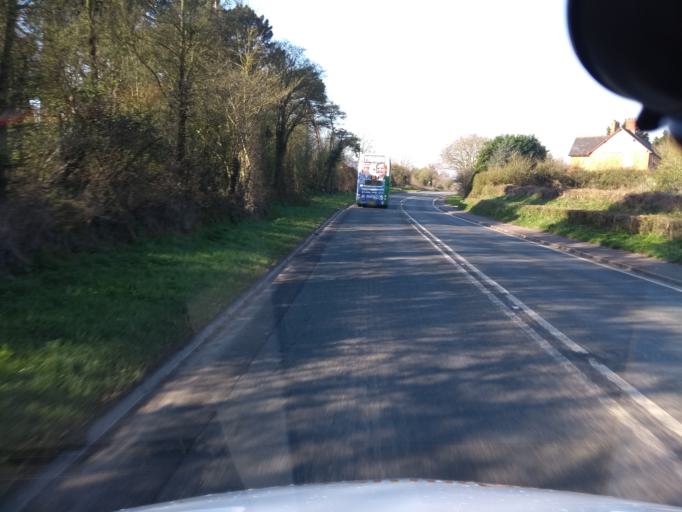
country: GB
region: England
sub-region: Somerset
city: Taunton
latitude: 51.0006
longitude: -3.1588
